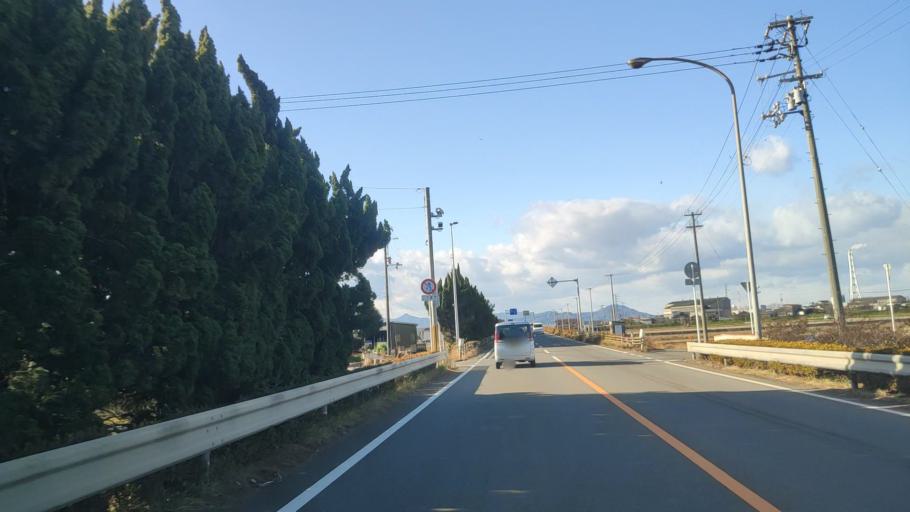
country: JP
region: Ehime
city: Saijo
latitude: 33.9168
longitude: 133.1287
